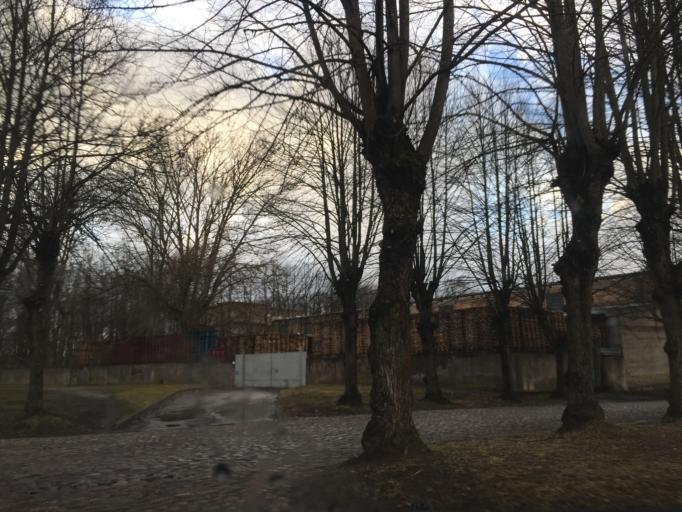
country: LV
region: Marupe
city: Marupe
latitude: 56.9427
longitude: 24.0498
